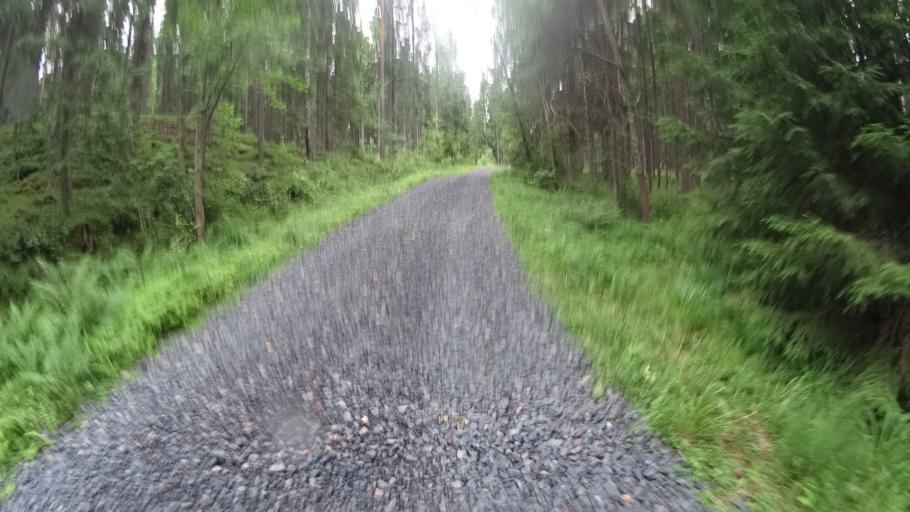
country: FI
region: Uusimaa
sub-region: Helsinki
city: Karkkila
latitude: 60.5832
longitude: 24.1511
